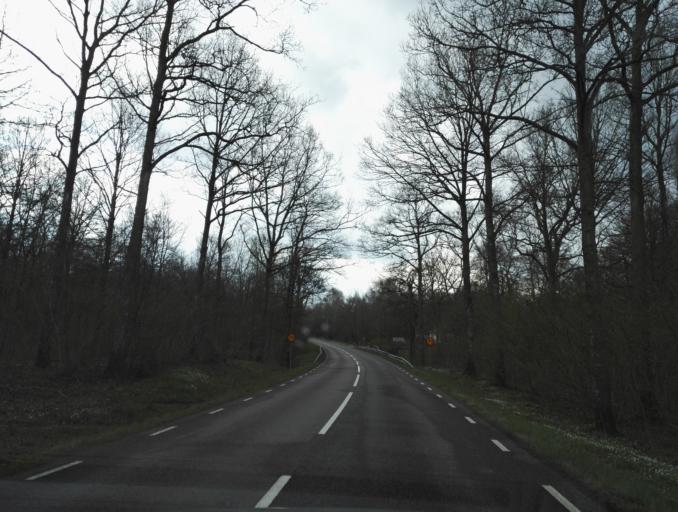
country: SE
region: Skane
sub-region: Svalovs Kommun
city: Kagerod
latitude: 55.9934
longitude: 13.0974
